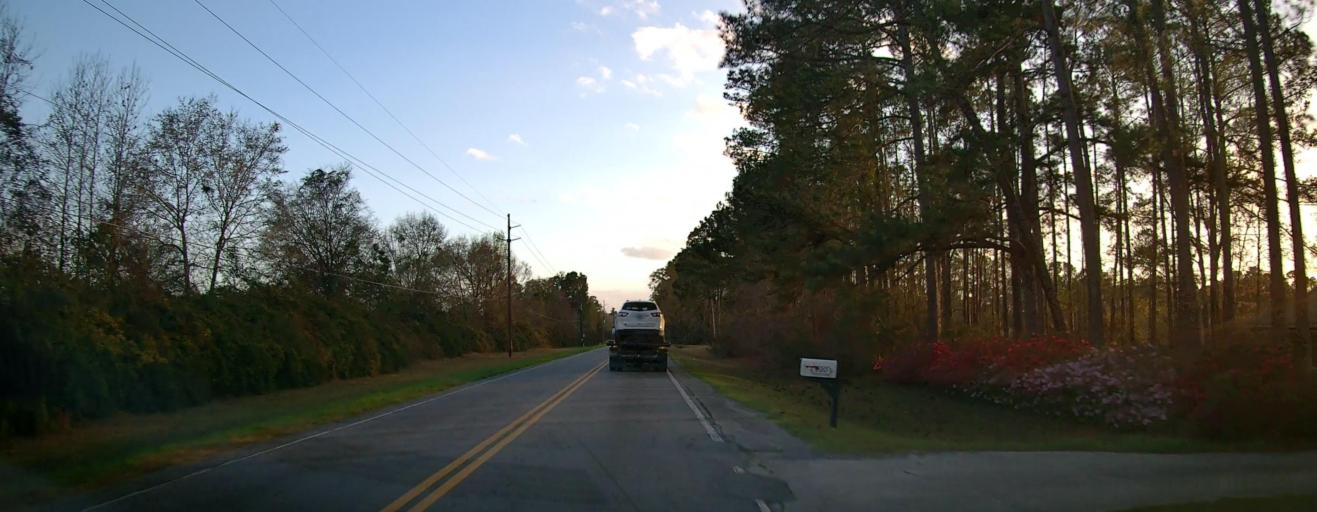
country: US
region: Georgia
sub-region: Chatham County
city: Bloomingdale
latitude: 32.1583
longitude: -81.3867
